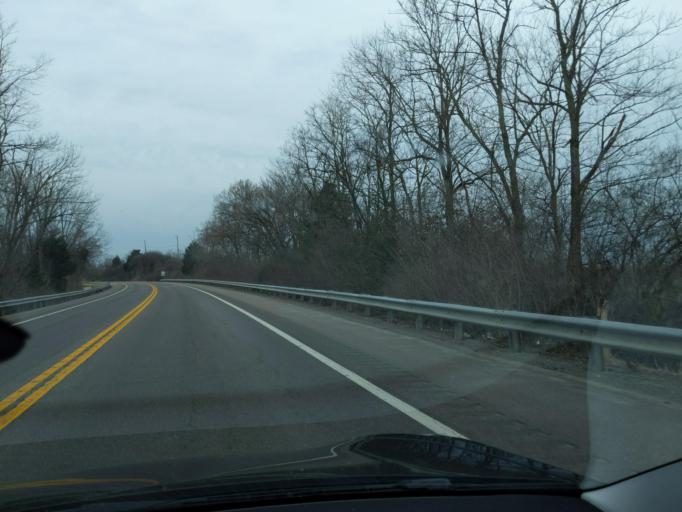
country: US
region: Kentucky
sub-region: Madison County
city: Richmond
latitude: 37.8814
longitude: -84.2950
